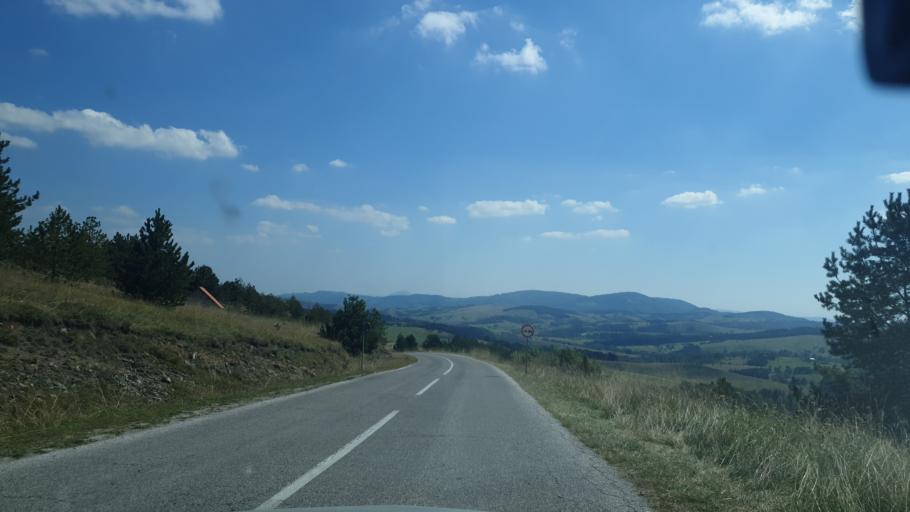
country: RS
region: Central Serbia
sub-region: Zlatiborski Okrug
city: Kosjeric
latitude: 44.0816
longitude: 20.0153
